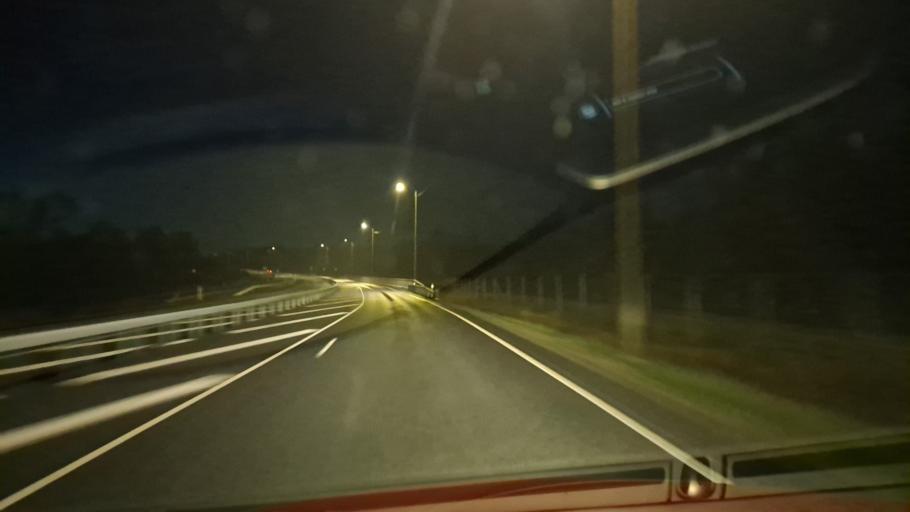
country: FI
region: Northern Ostrobothnia
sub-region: Oulunkaari
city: Kuivaniemi
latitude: 65.5605
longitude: 25.2362
